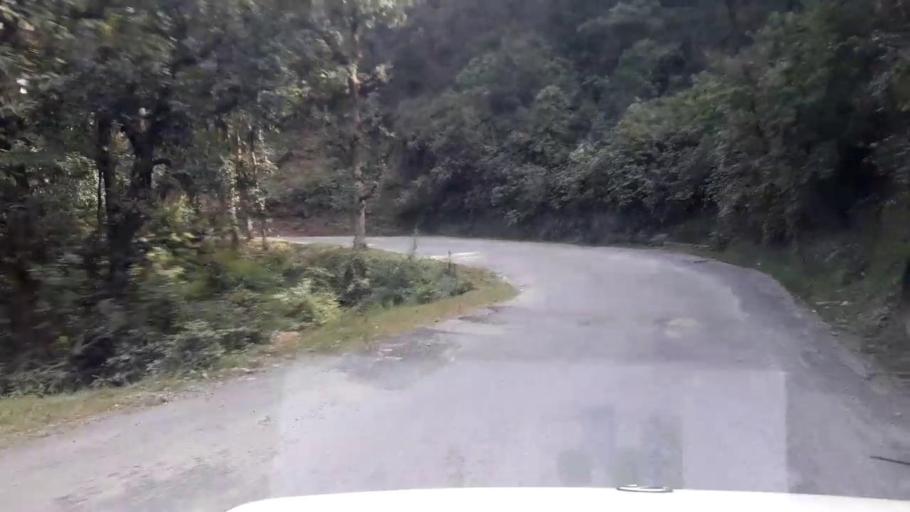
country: IN
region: Himachal Pradesh
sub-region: Shimla
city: Shimla
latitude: 31.0500
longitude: 77.1493
